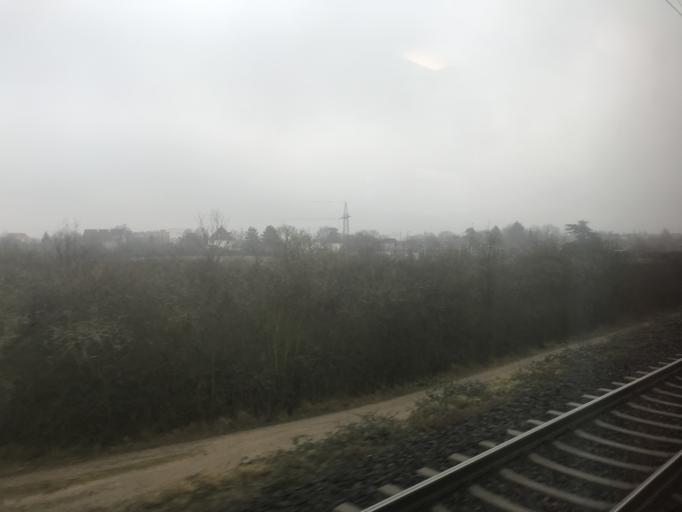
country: DE
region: Rheinland-Pfalz
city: Worms
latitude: 49.6519
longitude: 8.3537
